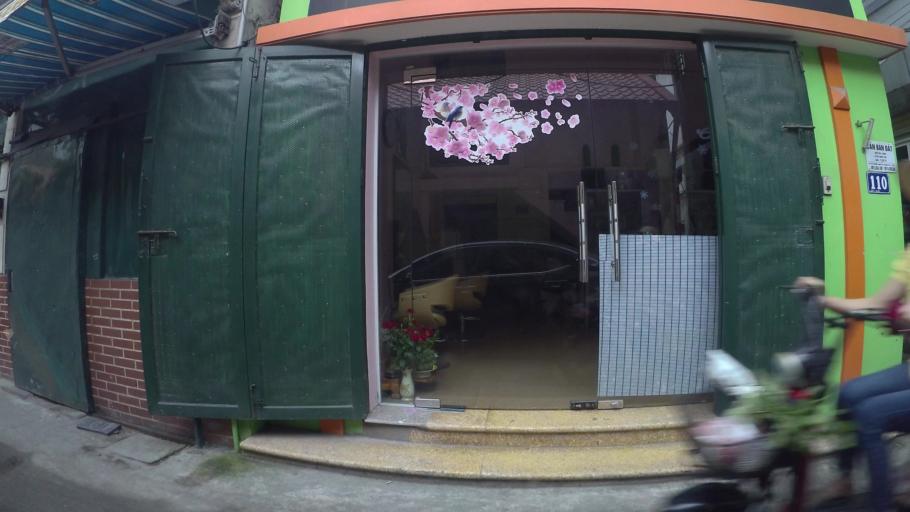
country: VN
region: Ha Noi
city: Van Dien
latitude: 20.9759
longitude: 105.8486
